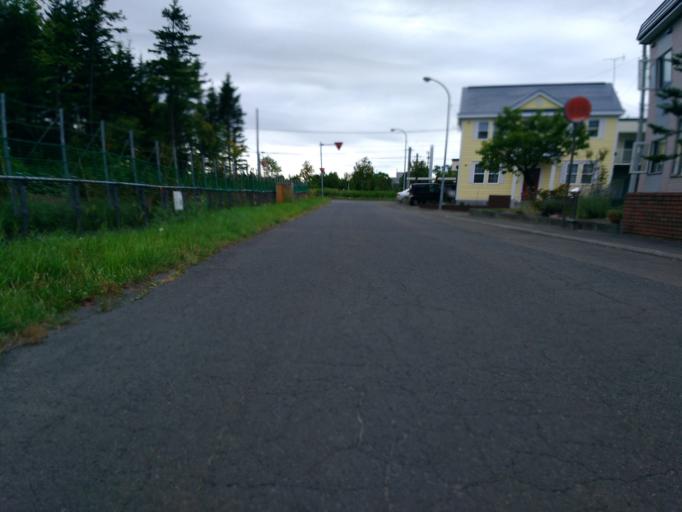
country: JP
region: Hokkaido
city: Ebetsu
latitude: 43.0846
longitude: 141.5204
